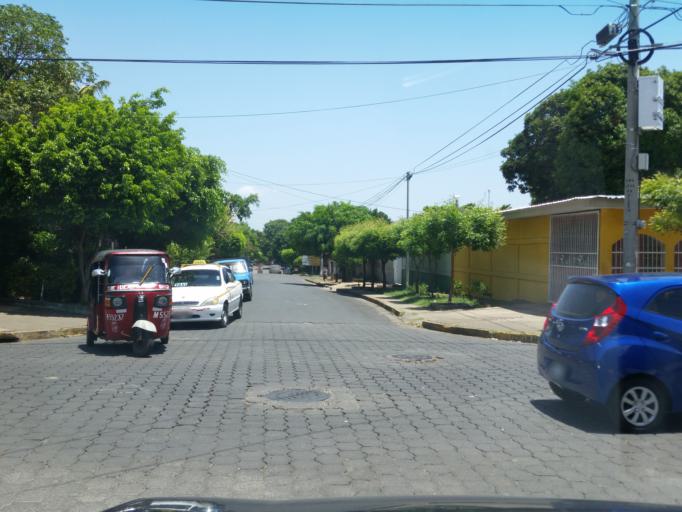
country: NI
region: Managua
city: Managua
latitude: 12.1182
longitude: -86.2380
